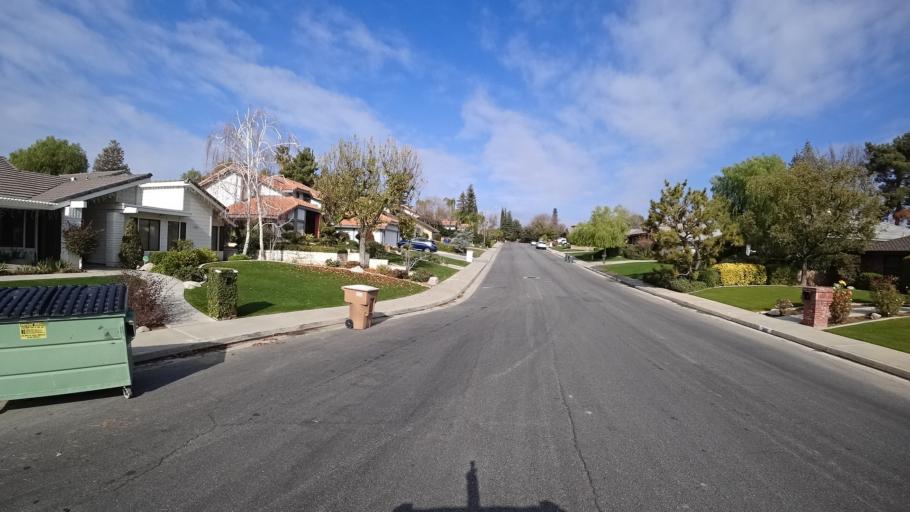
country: US
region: California
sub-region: Kern County
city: Bakersfield
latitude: 35.3942
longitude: -118.9314
